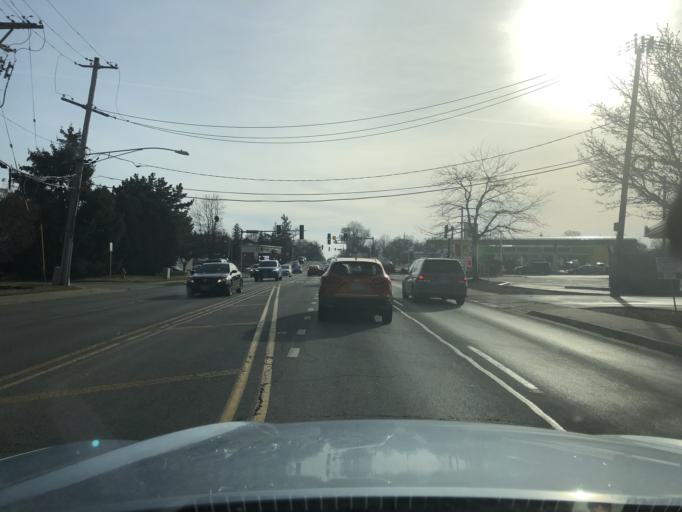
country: US
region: Illinois
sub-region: DuPage County
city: Roselle
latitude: 41.9858
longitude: -88.0803
